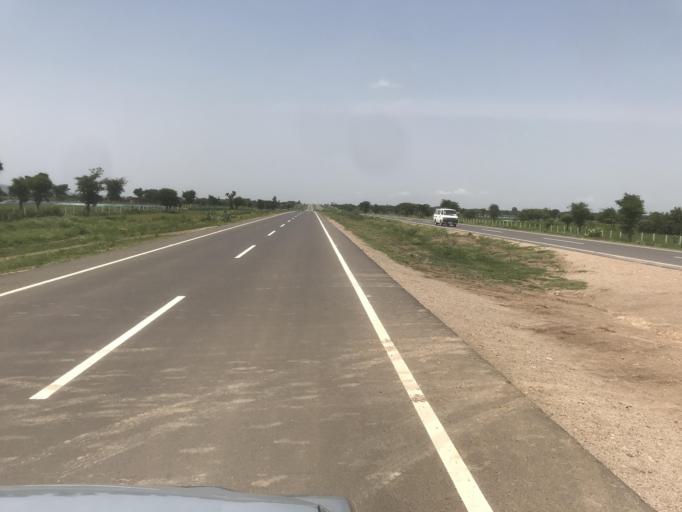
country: ET
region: Oromiya
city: Mojo
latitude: 8.3762
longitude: 39.0005
